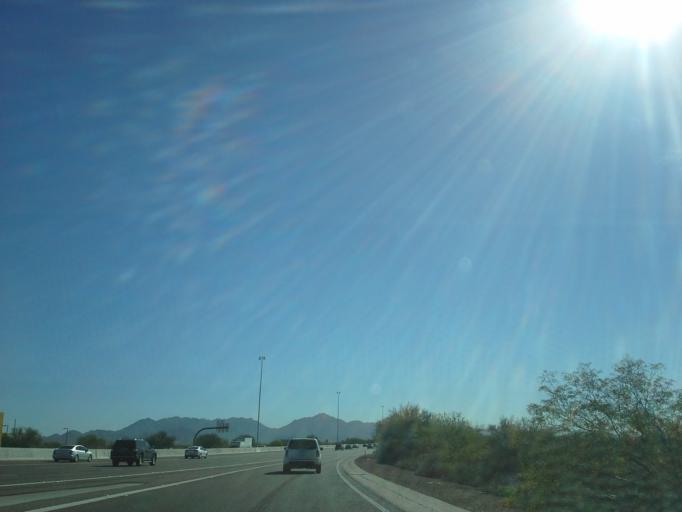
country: US
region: Arizona
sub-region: Maricopa County
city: Paradise Valley
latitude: 33.6726
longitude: -111.9730
